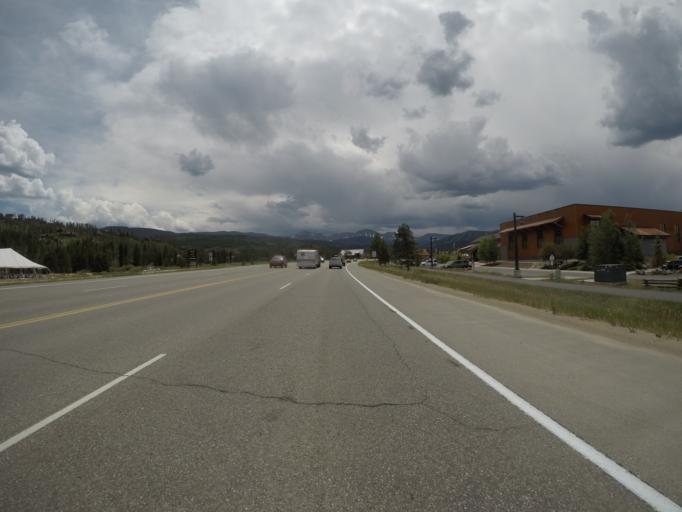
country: US
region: Colorado
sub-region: Grand County
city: Fraser
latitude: 39.9322
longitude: -105.7913
